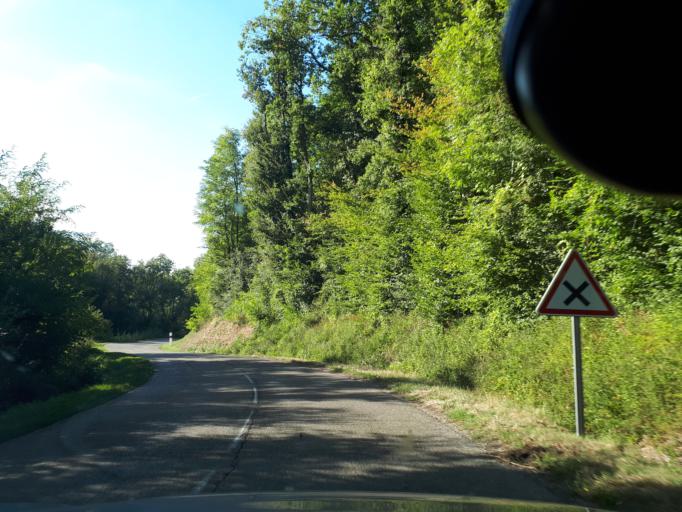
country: FR
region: Rhone-Alpes
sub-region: Departement de l'Isere
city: Maubec
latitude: 45.5397
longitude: 5.2541
